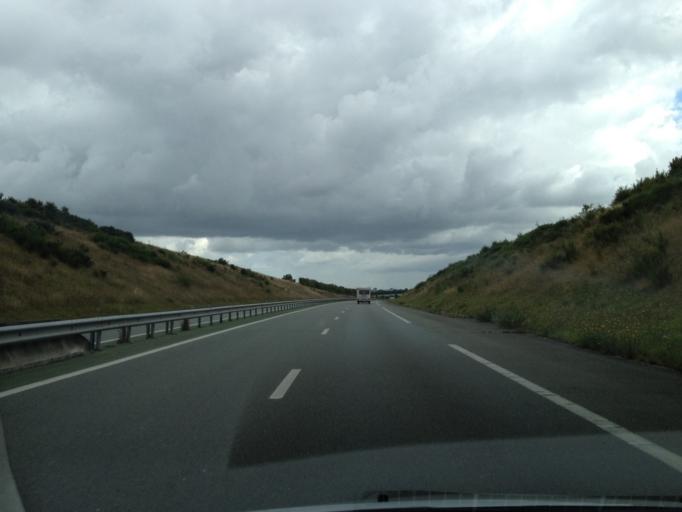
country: FR
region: Pays de la Loire
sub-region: Departement de Maine-et-Loire
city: Nuaille
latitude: 47.1077
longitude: -0.8269
